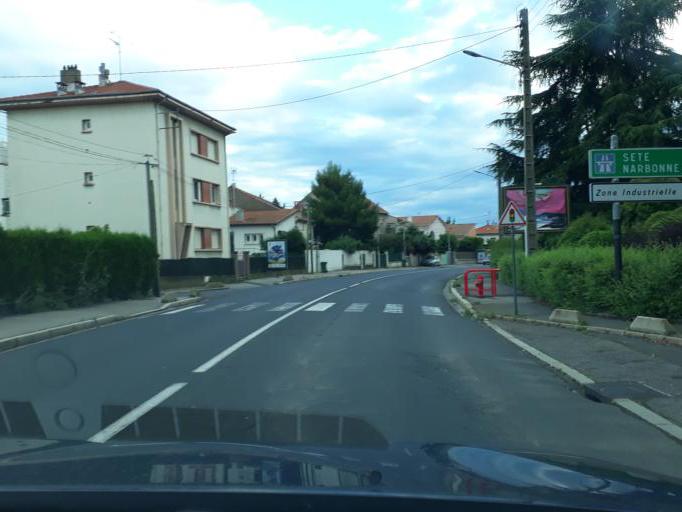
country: FR
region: Languedoc-Roussillon
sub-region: Departement de l'Herault
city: Beziers
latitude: 43.3362
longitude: 3.2359
